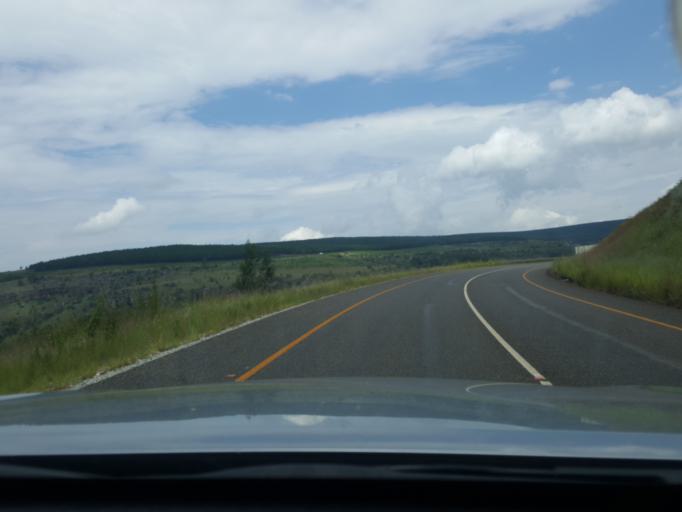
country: ZA
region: Mpumalanga
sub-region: Ehlanzeni District
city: Graksop
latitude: -25.1069
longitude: 30.8049
